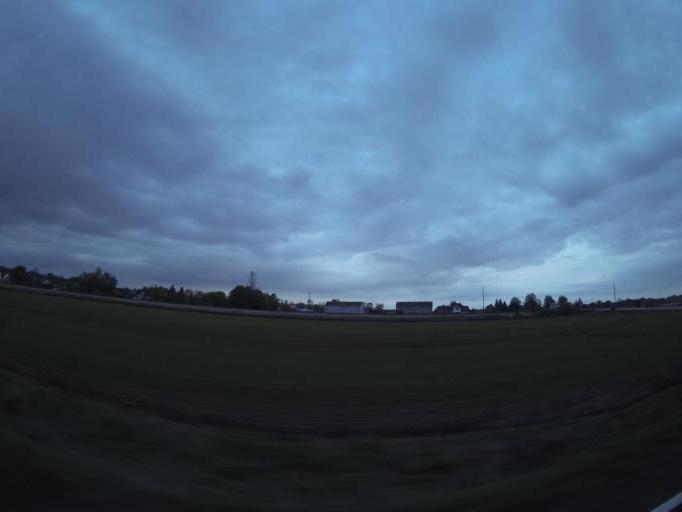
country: DE
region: Thuringia
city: Saara
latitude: 50.9208
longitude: 12.4412
